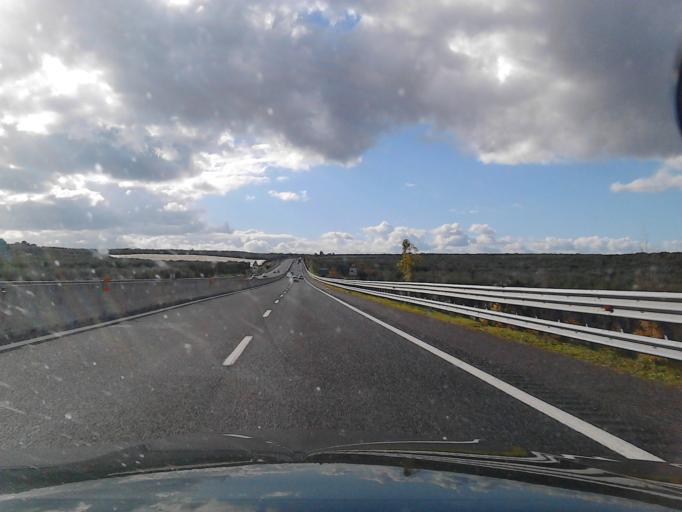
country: IT
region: Apulia
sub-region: Provincia di Barletta - Andria - Trani
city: Andria
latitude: 41.2577
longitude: 16.2393
